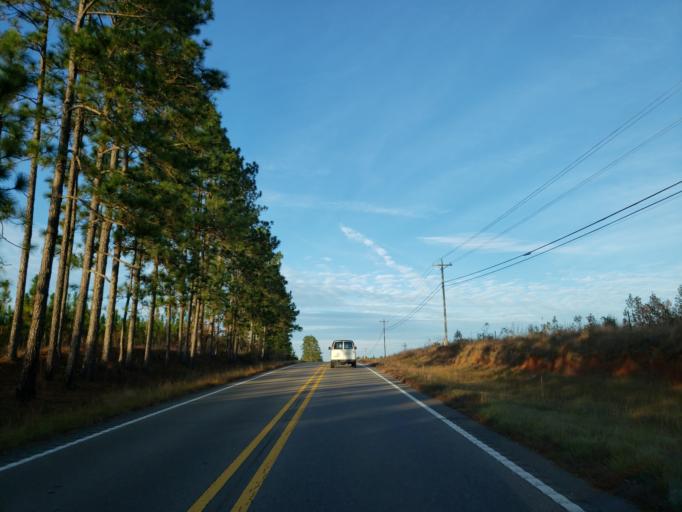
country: US
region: Mississippi
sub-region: Lamar County
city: Purvis
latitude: 31.2231
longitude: -89.3555
